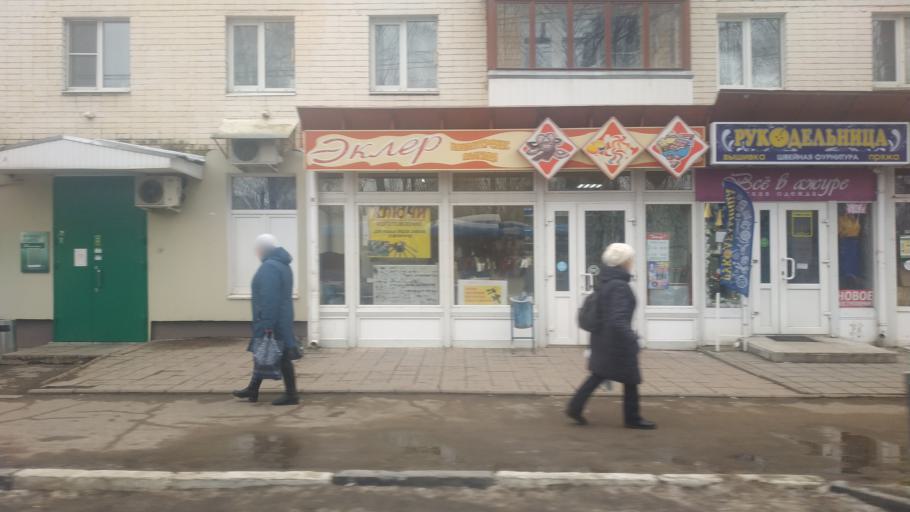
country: RU
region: Tverskaya
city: Tver
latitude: 56.8705
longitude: 35.8881
